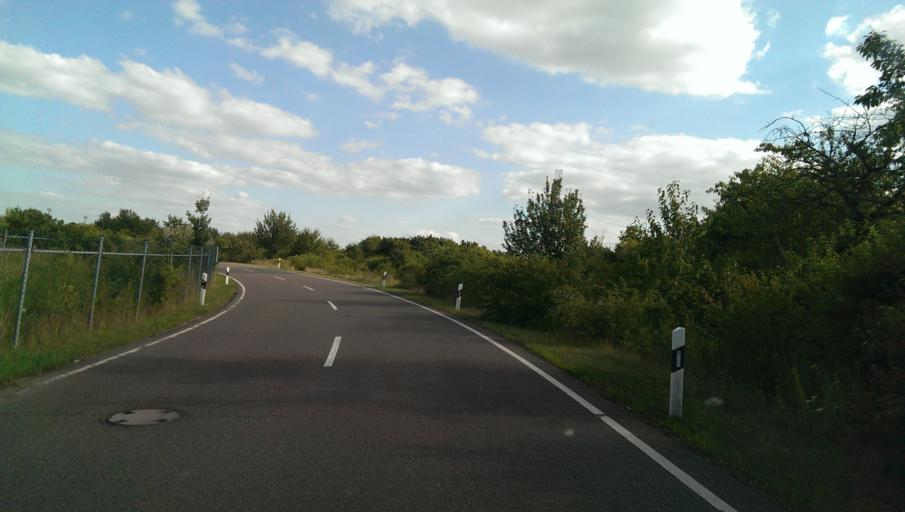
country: DE
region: Saxony
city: Rackwitz
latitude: 51.4202
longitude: 12.3802
